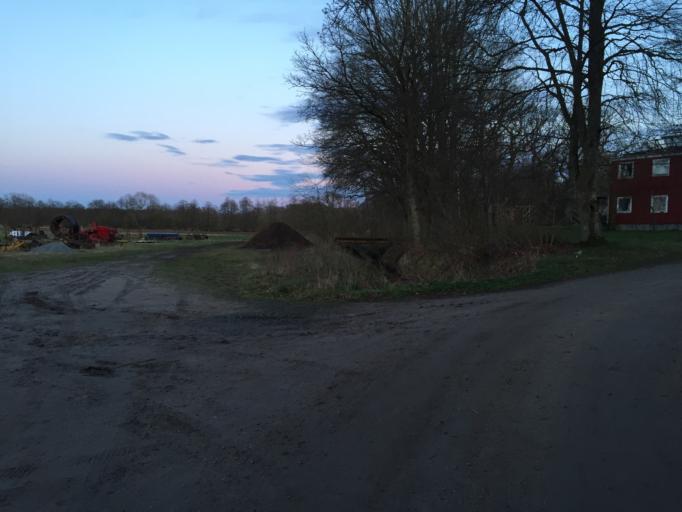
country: SE
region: Skane
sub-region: Lunds Kommun
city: Veberod
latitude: 55.6364
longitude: 13.5187
